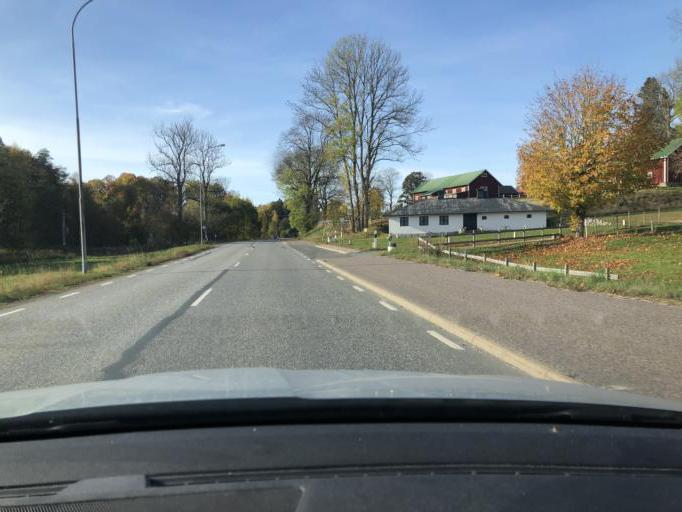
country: SE
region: Joenkoeping
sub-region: Jonkopings Kommun
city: Jonkoping
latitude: 57.7717
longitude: 14.1128
